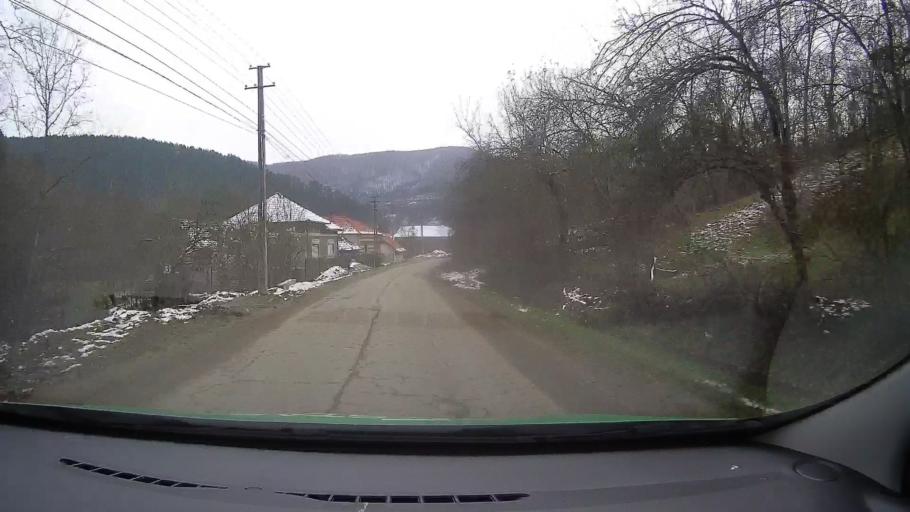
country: RO
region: Hunedoara
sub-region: Comuna Geoagiu
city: Geoagiu
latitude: 45.9777
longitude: 23.1679
